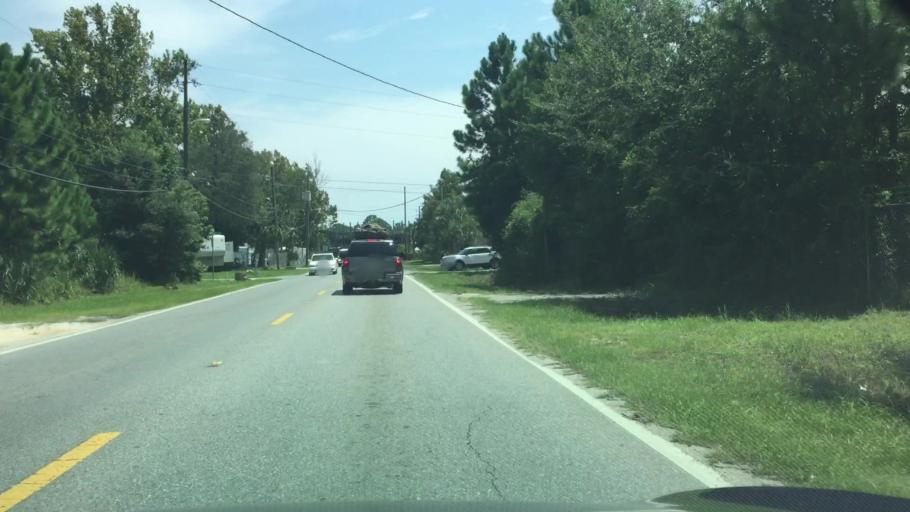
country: US
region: Florida
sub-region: Bay County
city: Panama City Beach
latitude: 30.1823
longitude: -85.7927
